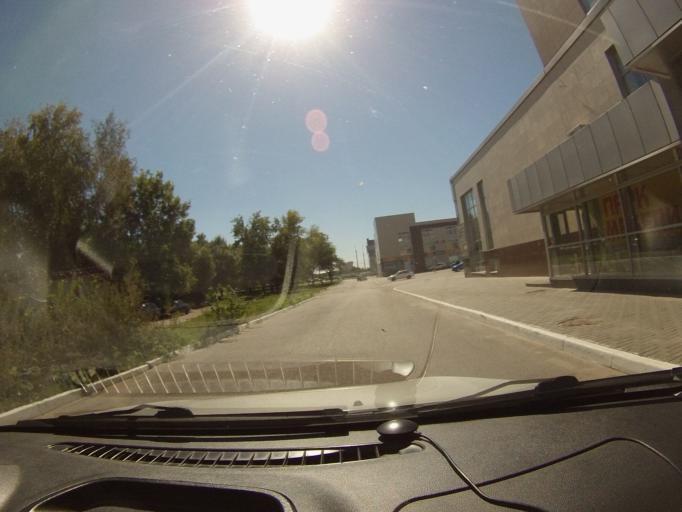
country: RU
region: Tambov
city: Tambov
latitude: 52.7595
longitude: 41.4382
